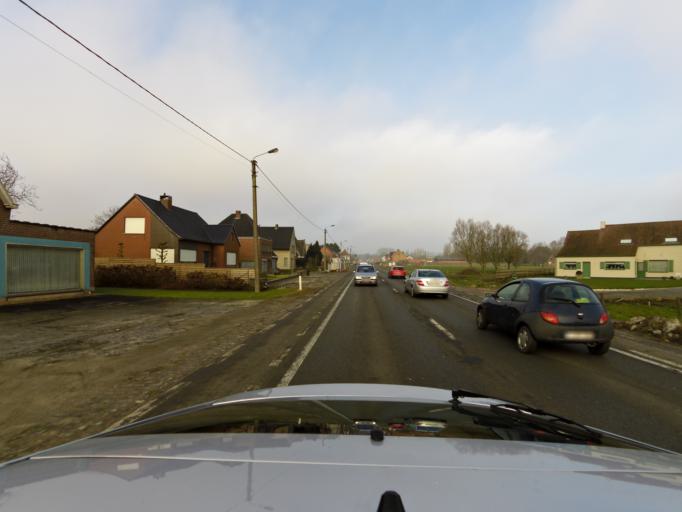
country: BE
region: Flanders
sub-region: Provincie West-Vlaanderen
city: Torhout
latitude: 51.0733
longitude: 3.0769
